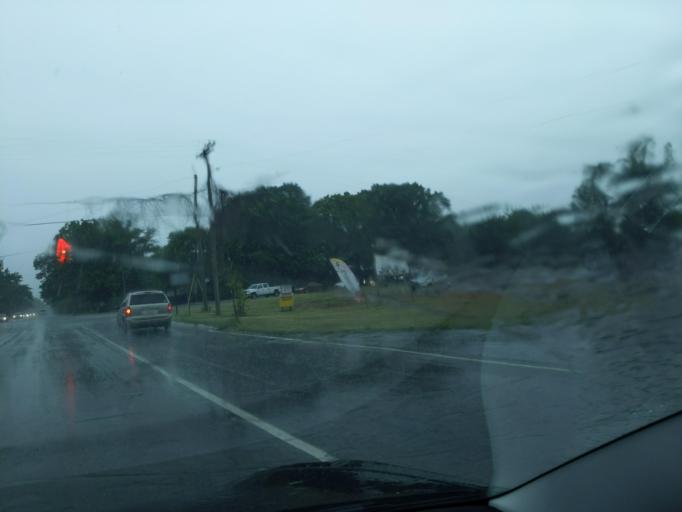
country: US
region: Michigan
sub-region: Muskegon County
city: Fruitport
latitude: 43.1502
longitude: -86.1653
